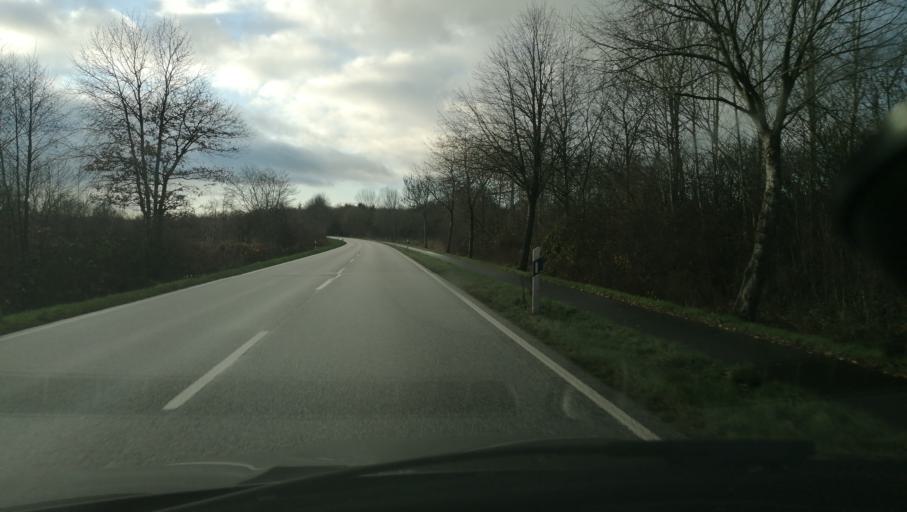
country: DE
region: Schleswig-Holstein
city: Sarzbuttel
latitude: 54.1114
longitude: 9.2092
